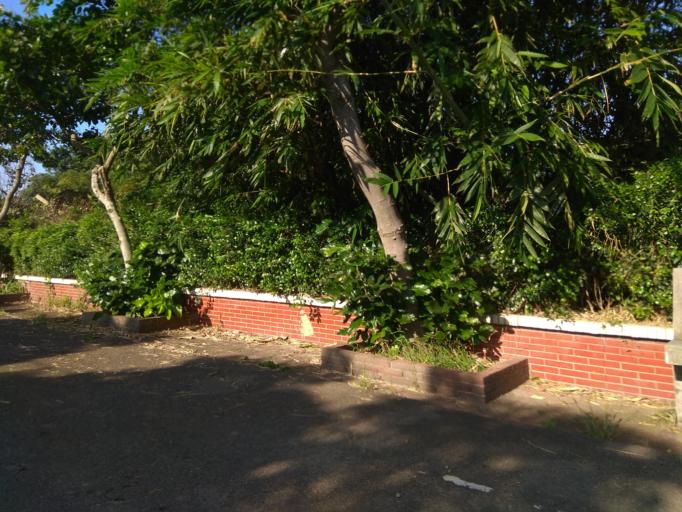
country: TW
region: Taiwan
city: Taoyuan City
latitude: 25.0506
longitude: 121.2288
